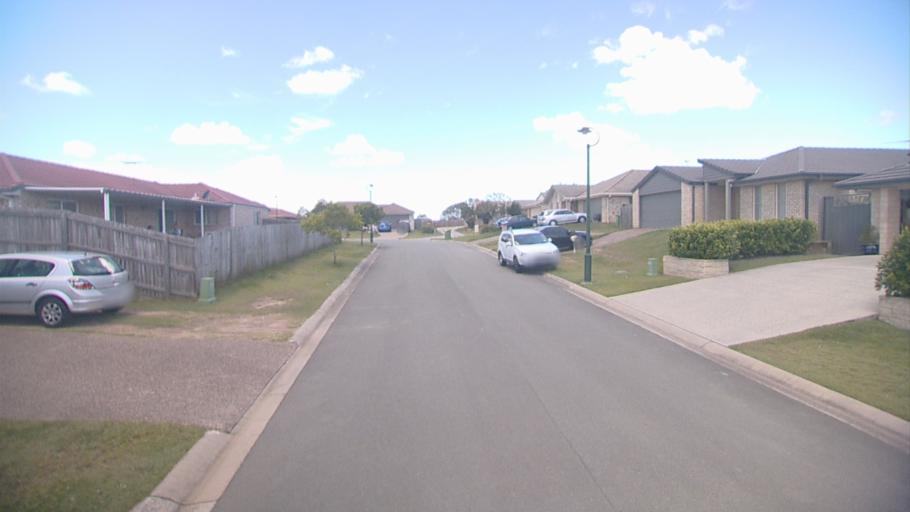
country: AU
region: Queensland
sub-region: Gold Coast
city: Yatala
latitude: -27.6940
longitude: 153.2211
